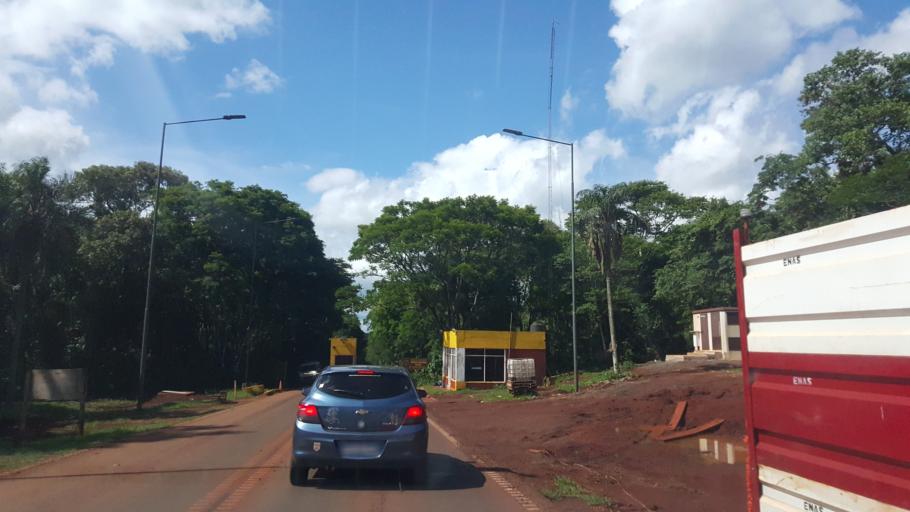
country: AR
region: Misiones
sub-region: Departamento de Iguazu
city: Puerto Iguazu
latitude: -25.7293
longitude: -54.4702
